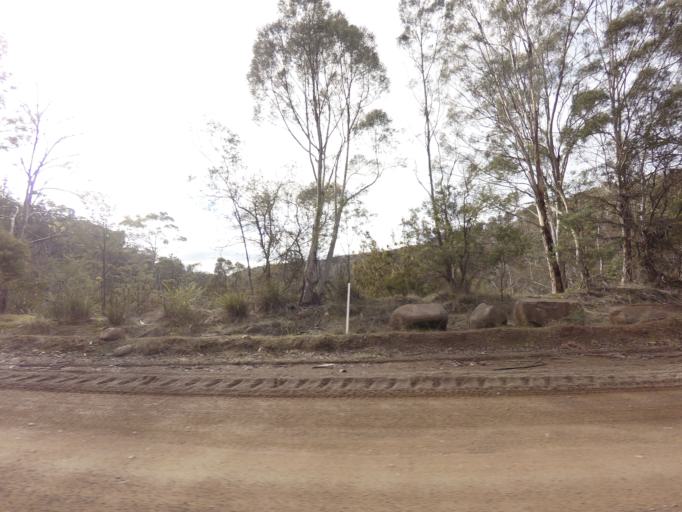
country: AU
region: Tasmania
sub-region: Derwent Valley
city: New Norfolk
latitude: -42.7427
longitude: 146.8669
